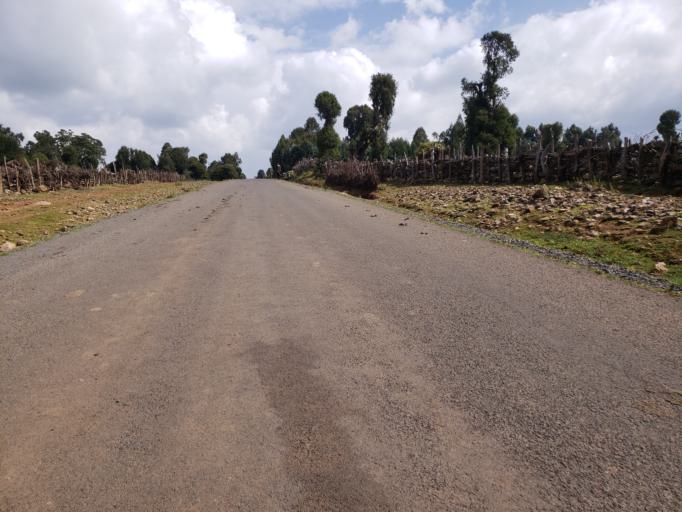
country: ET
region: Oromiya
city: Dodola
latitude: 6.8689
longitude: 39.3887
